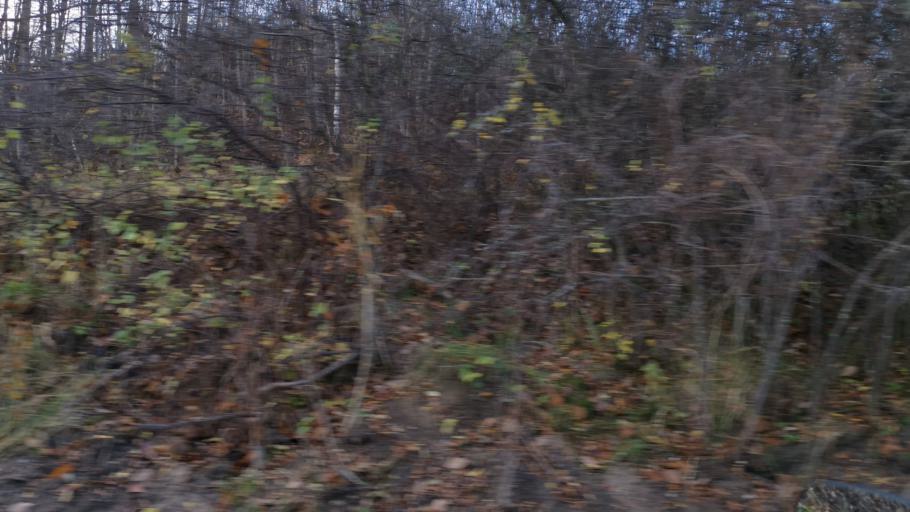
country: SE
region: Vaestra Goetaland
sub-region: Munkedals Kommun
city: Munkedal
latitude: 58.4674
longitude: 11.6784
